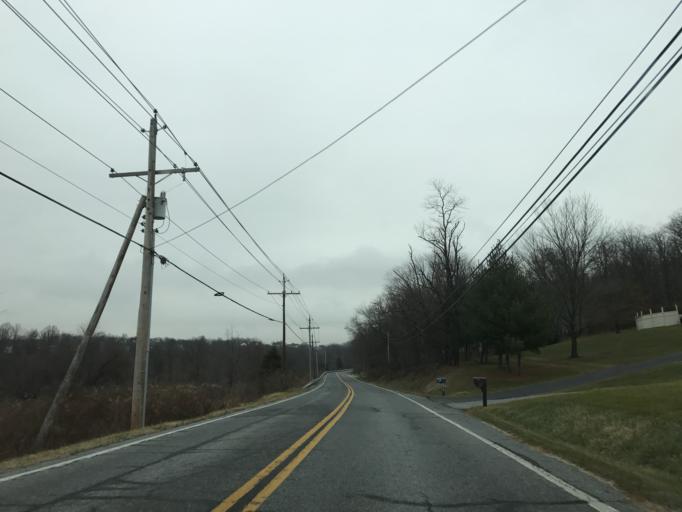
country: US
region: Maryland
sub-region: Carroll County
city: Westminster
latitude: 39.5709
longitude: -77.0173
